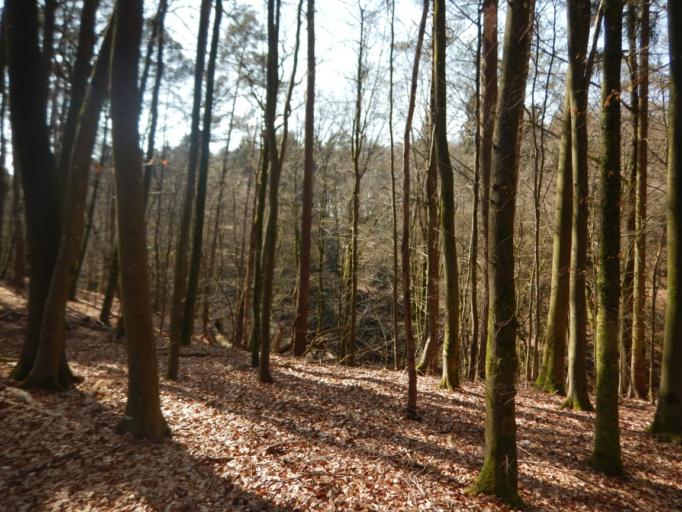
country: LU
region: Grevenmacher
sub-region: Canton d'Echternach
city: Consdorf
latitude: 49.7783
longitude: 6.3578
